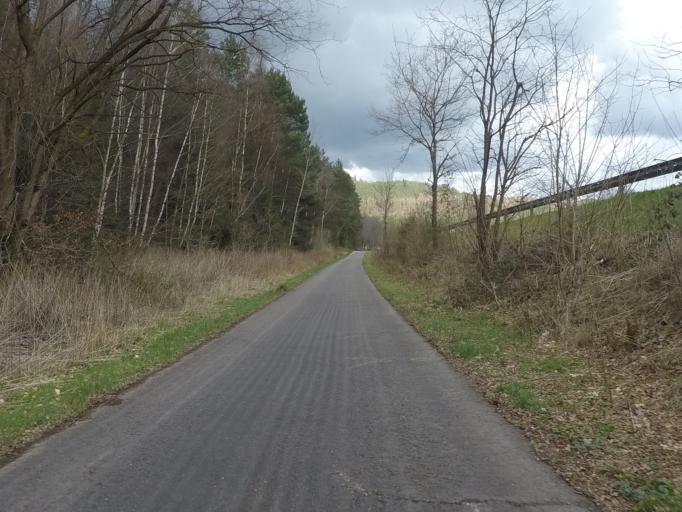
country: DE
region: Rheinland-Pfalz
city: Munchweiler an der Rodalbe
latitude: 49.2264
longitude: 7.6919
